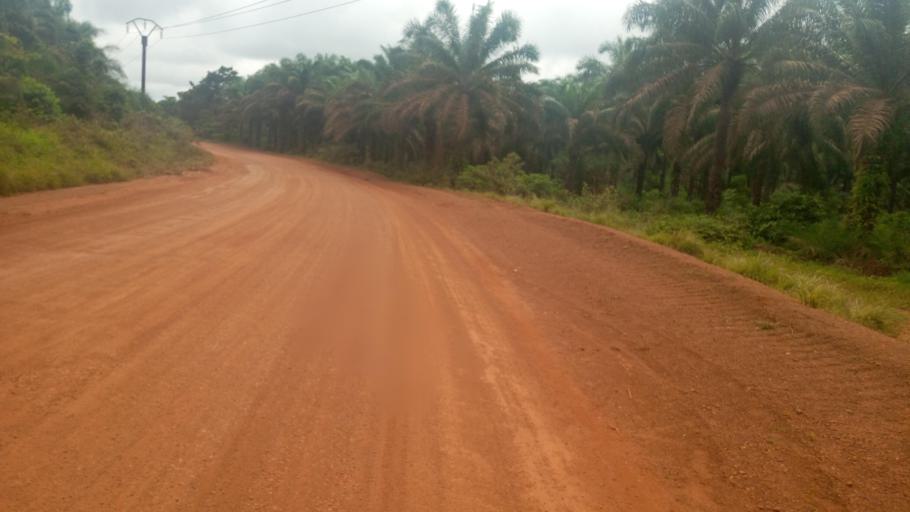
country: SL
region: Southern Province
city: Mogbwemo
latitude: 7.7266
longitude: -12.2775
